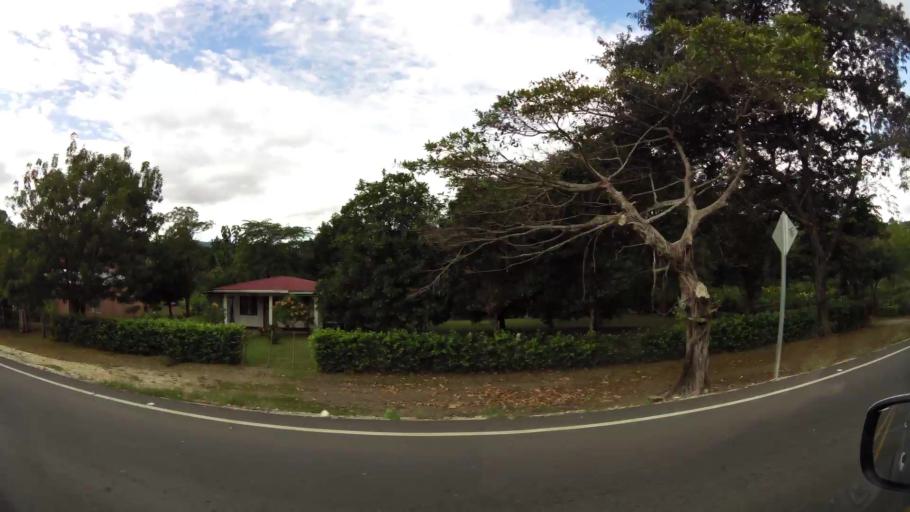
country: CR
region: Guanacaste
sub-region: Canton de Nicoya
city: Nicoya
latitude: 10.1440
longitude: -85.3227
